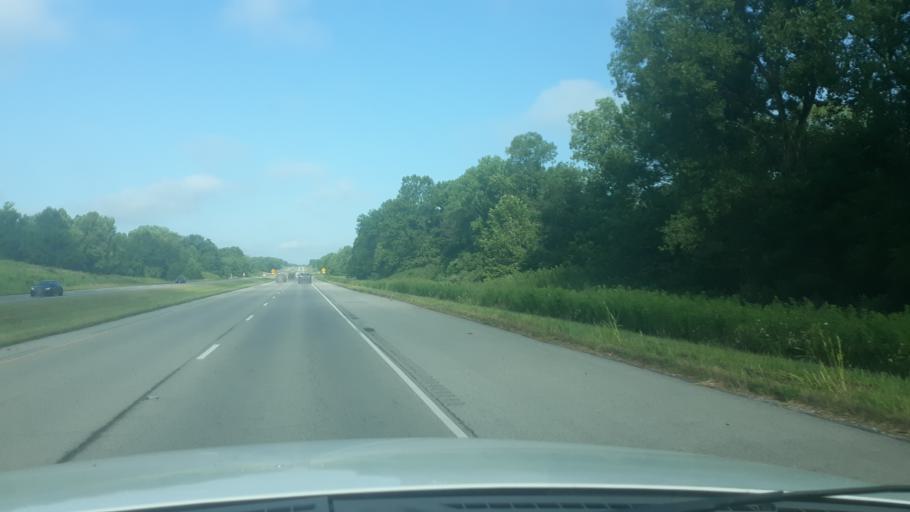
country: US
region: Illinois
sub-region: Saline County
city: Carrier Mills
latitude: 37.7308
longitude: -88.7470
